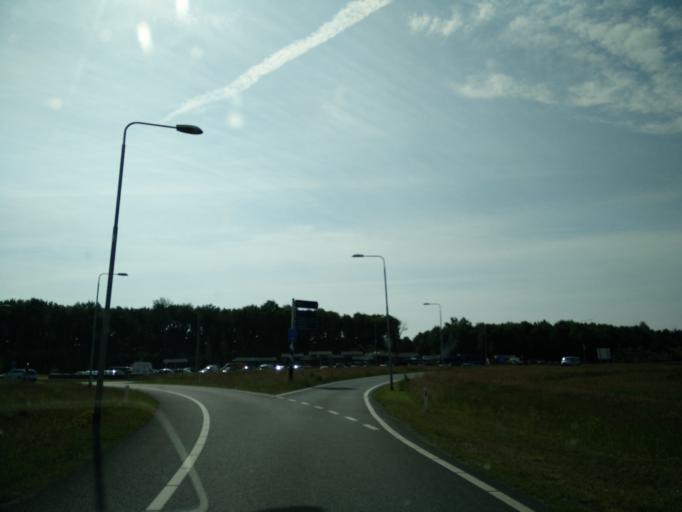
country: NL
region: Drenthe
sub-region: Gemeente Aa en Hunze
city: Anloo
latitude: 53.0099
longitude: 6.7491
